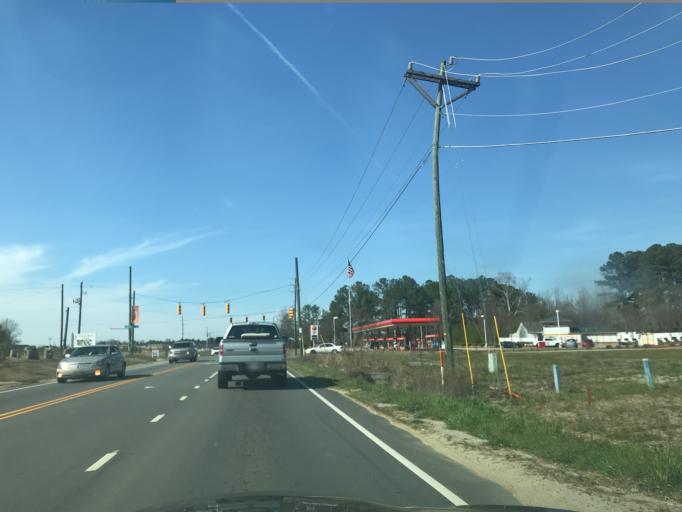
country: US
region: North Carolina
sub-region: Harnett County
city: Angier
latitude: 35.5363
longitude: -78.7464
